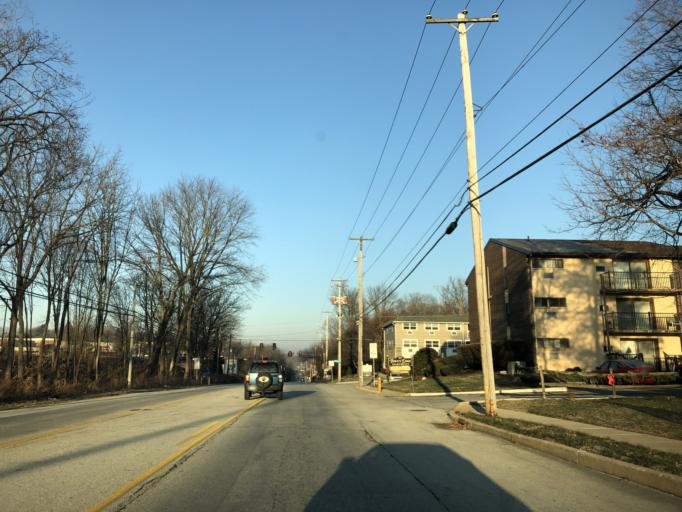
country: US
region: Pennsylvania
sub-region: Chester County
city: West Chester
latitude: 39.9601
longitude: -75.6185
